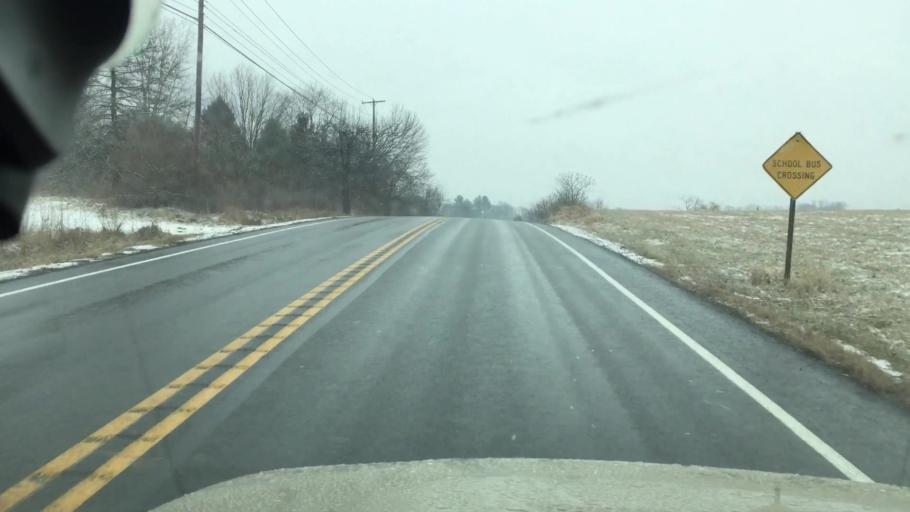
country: US
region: Pennsylvania
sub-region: Luzerne County
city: Nescopeck
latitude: 41.0524
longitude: -76.1655
